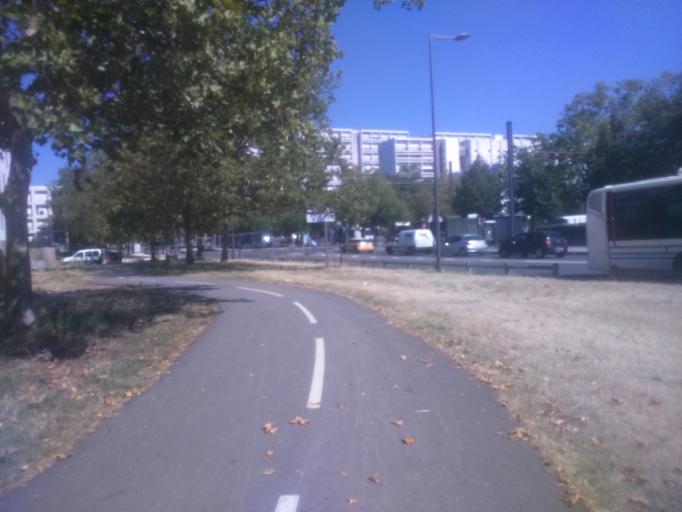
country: FR
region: Aquitaine
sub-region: Departement de la Gironde
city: Le Bouscat
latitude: 44.8742
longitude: -0.5760
